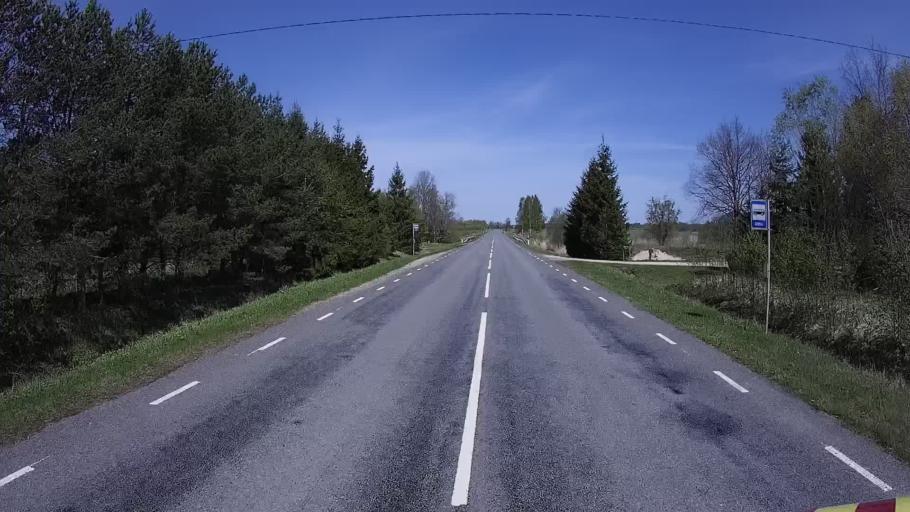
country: EE
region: Laeaene
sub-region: Lihula vald
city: Lihula
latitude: 58.6541
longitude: 23.8375
